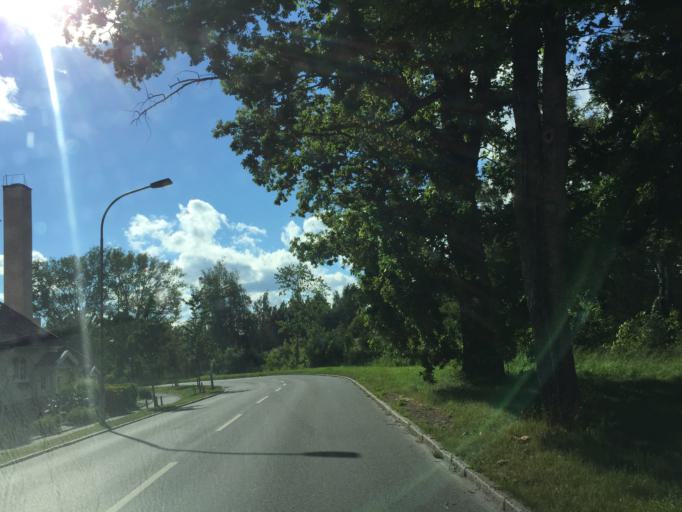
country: SE
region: OErebro
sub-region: Orebro Kommun
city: Orebro
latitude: 59.2948
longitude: 15.2314
